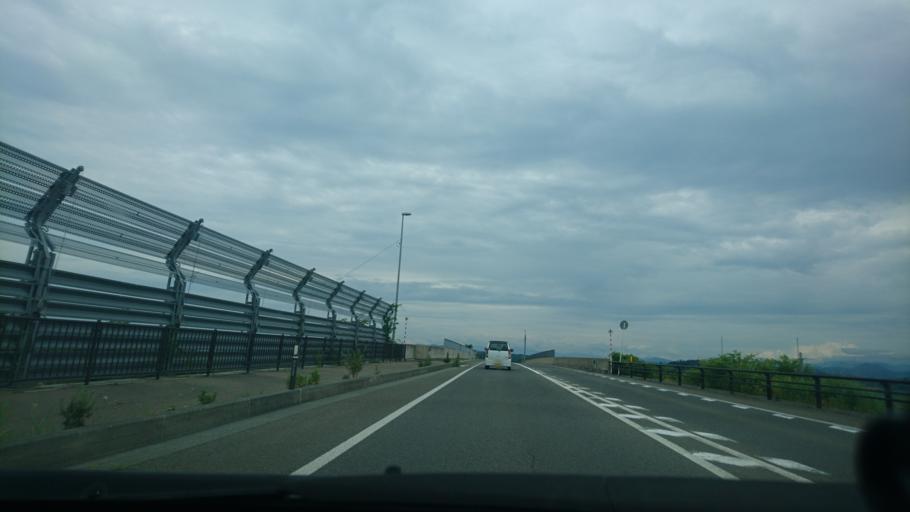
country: JP
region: Akita
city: Omagari
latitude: 39.4904
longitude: 140.4516
